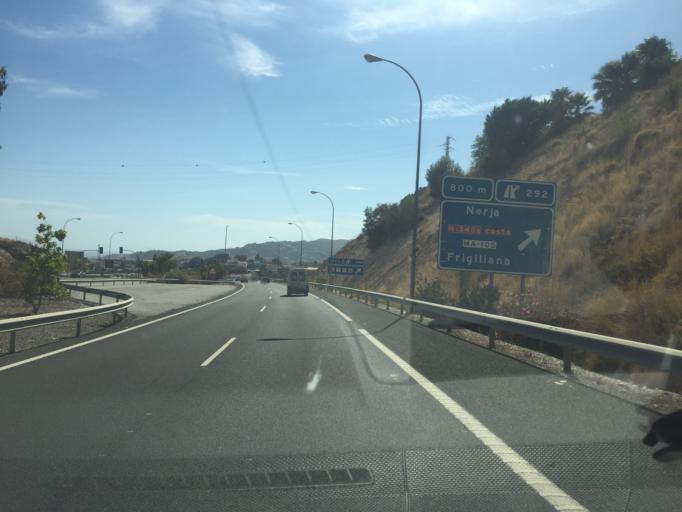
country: ES
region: Andalusia
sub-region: Provincia de Malaga
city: Nerja
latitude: 36.7675
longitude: -3.8738
